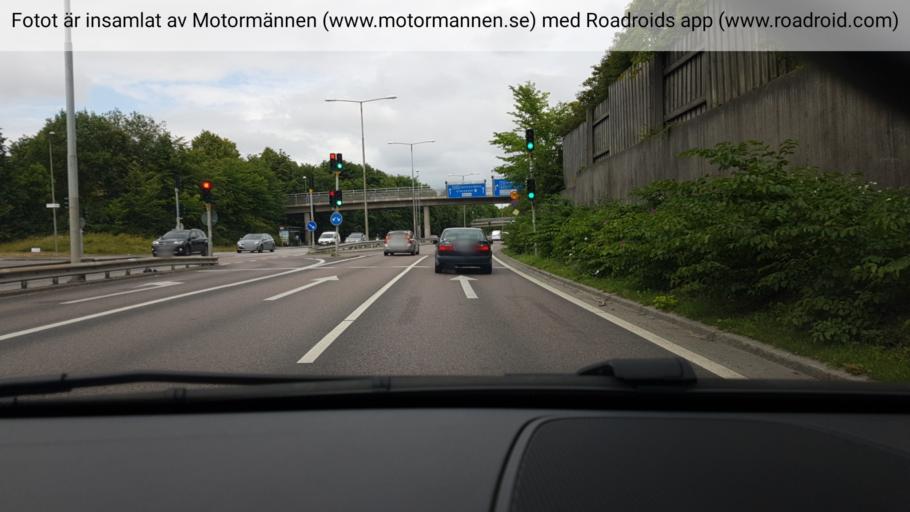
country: SE
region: Stockholm
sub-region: Stockholms Kommun
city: Arsta
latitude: 59.2794
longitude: 18.0343
